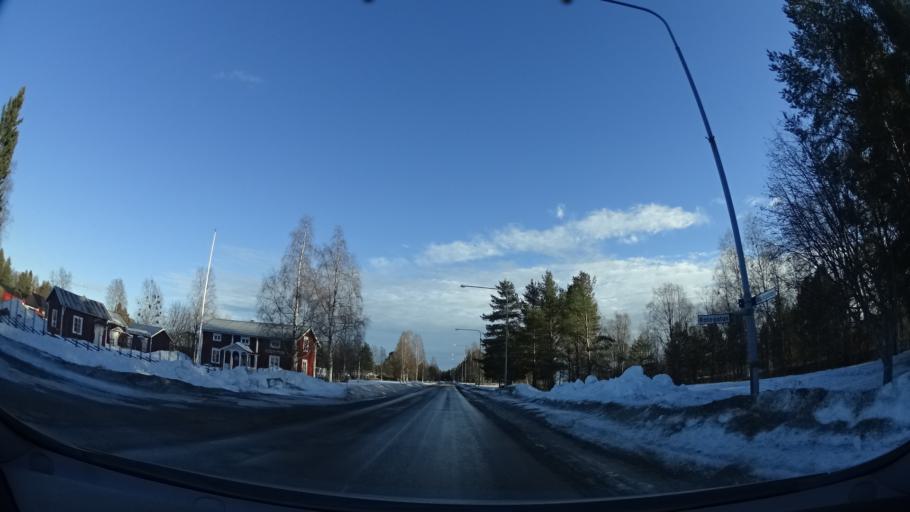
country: SE
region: Vaesterbotten
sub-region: Skelleftea Kommun
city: Byske
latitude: 64.9495
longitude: 21.2212
